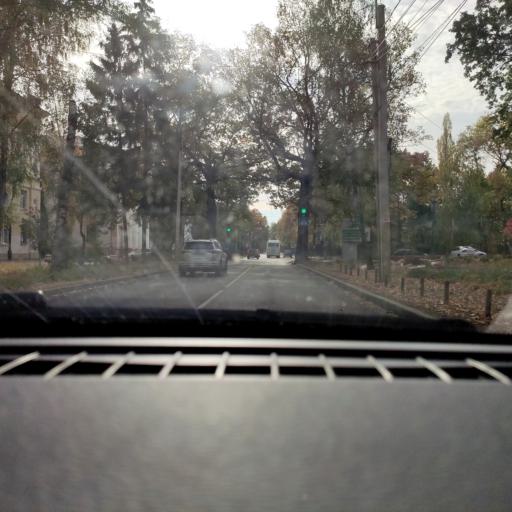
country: RU
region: Voronezj
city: Voronezh
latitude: 51.7198
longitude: 39.2195
